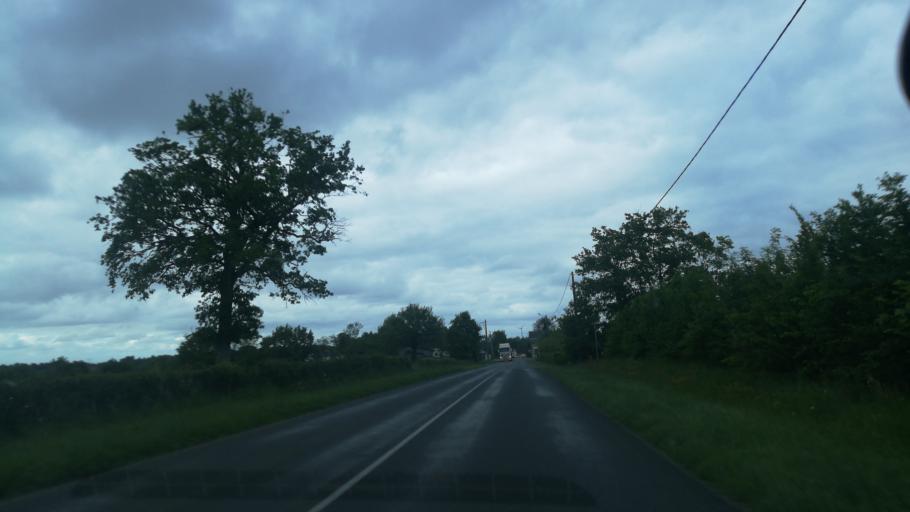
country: FR
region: Poitou-Charentes
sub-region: Departement des Deux-Sevres
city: Courlay
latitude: 46.7639
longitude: -0.5302
